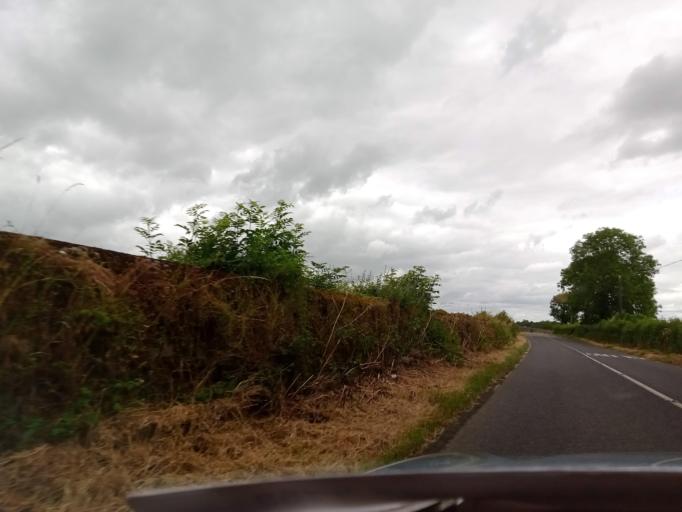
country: IE
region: Leinster
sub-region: Kilkenny
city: Thomastown
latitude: 52.5074
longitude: -7.2168
